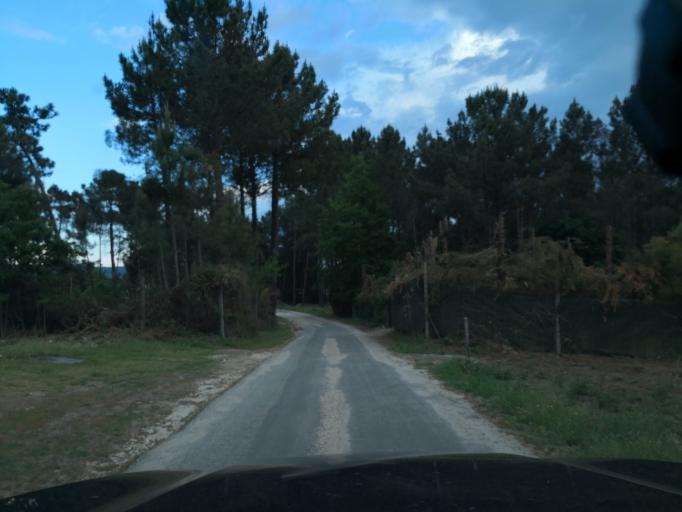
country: PT
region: Vila Real
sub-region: Vila Real
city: Vila Real
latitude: 41.3209
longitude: -7.7503
